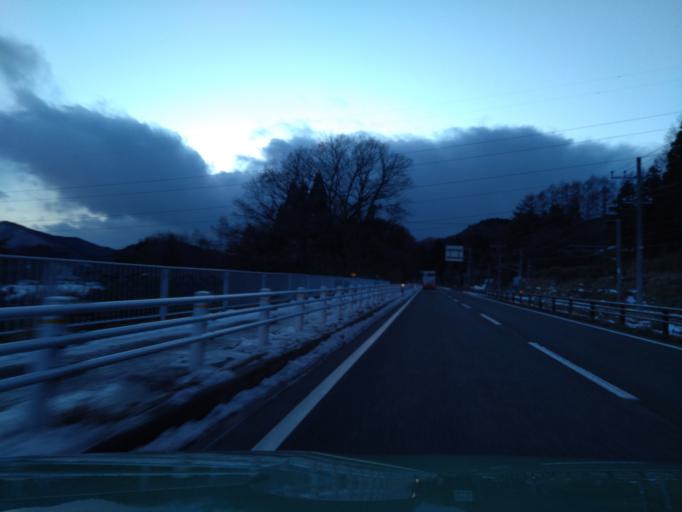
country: JP
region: Iwate
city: Shizukuishi
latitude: 39.6918
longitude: 140.9286
